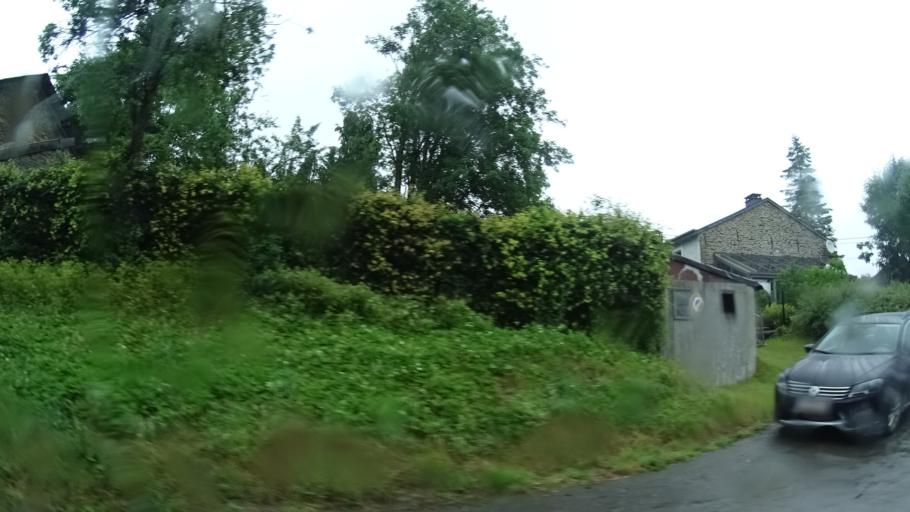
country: BE
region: Wallonia
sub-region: Province de Namur
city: Bievre
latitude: 49.9500
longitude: 5.0628
